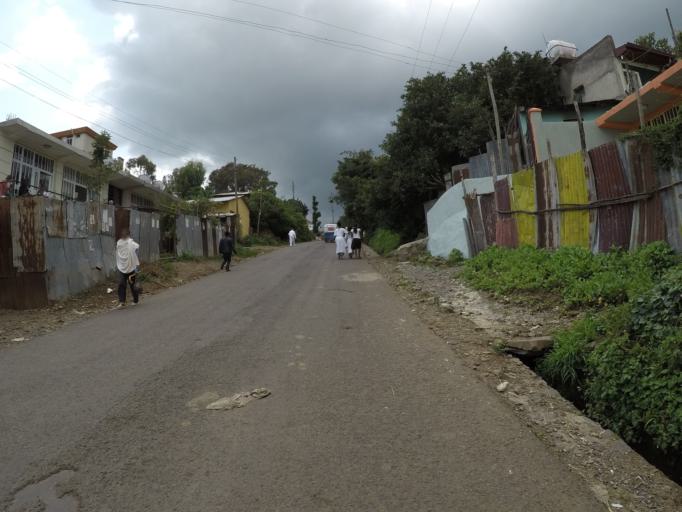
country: ET
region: Amhara
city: Gondar
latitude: 12.6147
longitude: 37.4753
